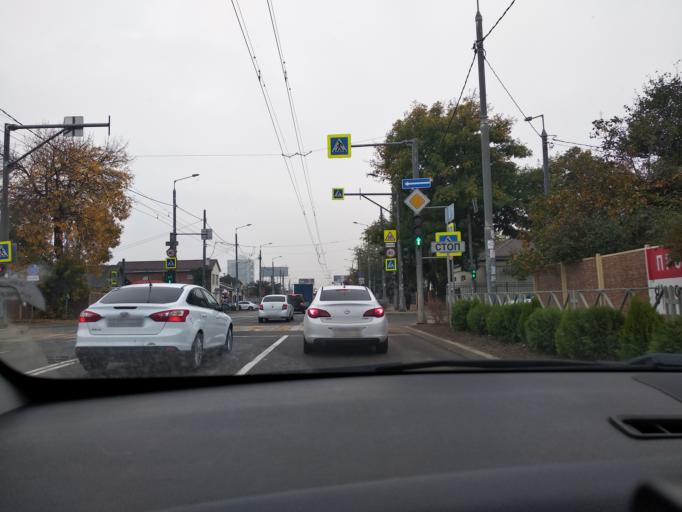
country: RU
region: Krasnodarskiy
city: Krasnodar
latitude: 45.0420
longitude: 38.9562
